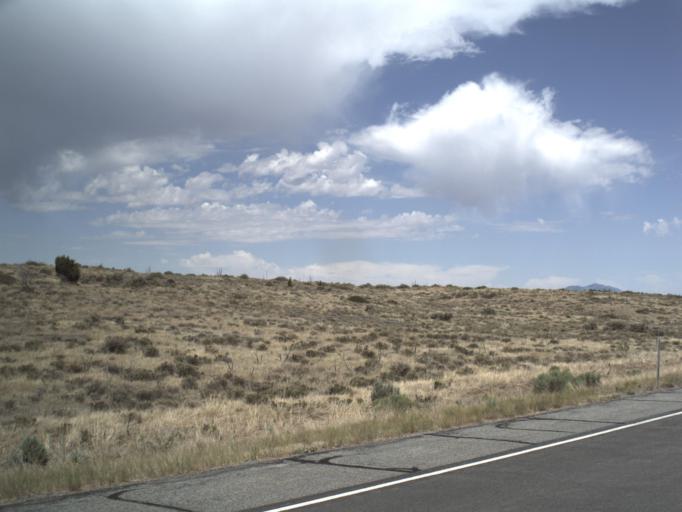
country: US
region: Utah
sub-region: Utah County
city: Genola
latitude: 39.9775
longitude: -112.2598
